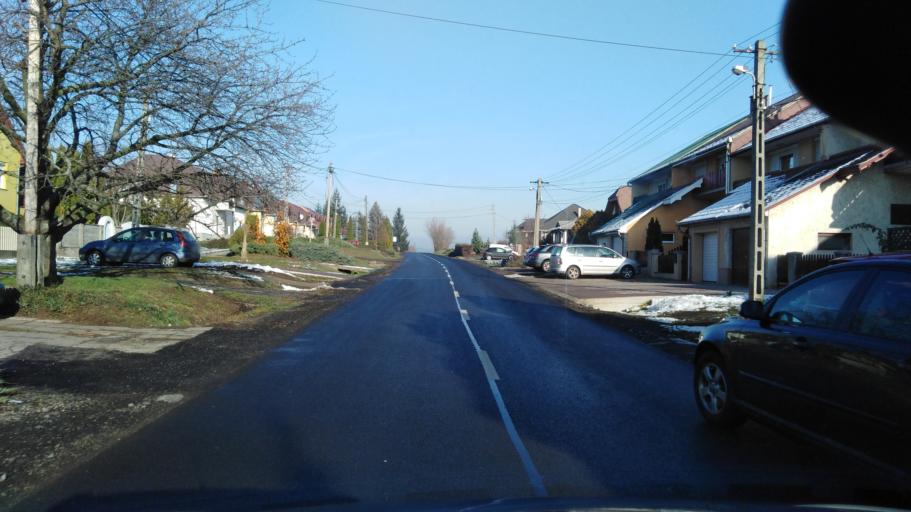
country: HU
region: Nograd
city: Paszto
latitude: 47.9298
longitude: 19.7038
